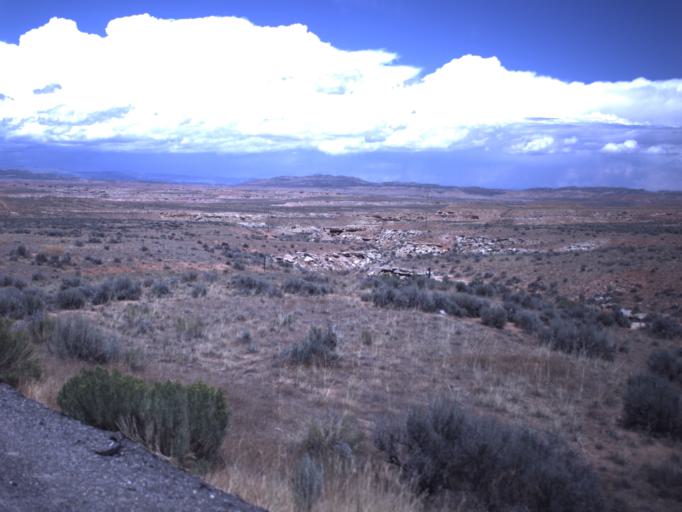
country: US
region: Utah
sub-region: Uintah County
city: Maeser
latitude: 40.3016
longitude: -109.6884
